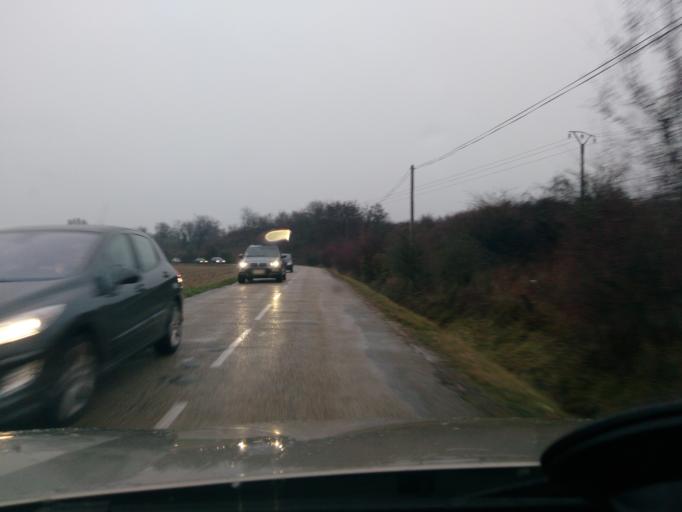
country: FR
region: Rhone-Alpes
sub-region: Departement de la Drome
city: Montelimar
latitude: 44.5360
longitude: 4.7200
